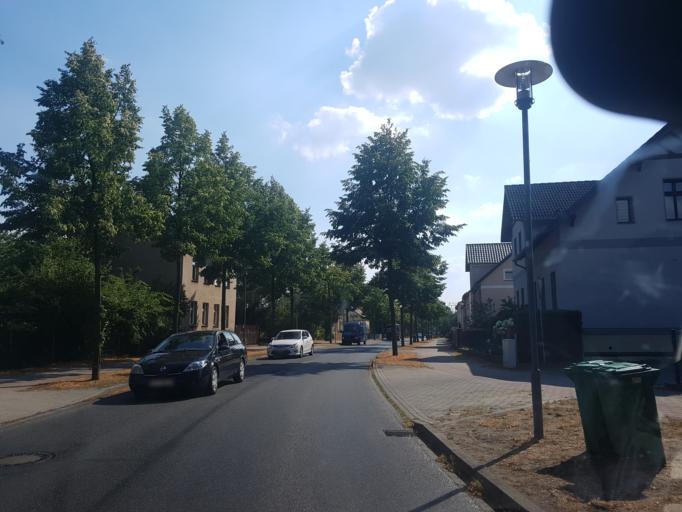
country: DE
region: Brandenburg
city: Grossbeeren
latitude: 52.3493
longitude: 13.3072
